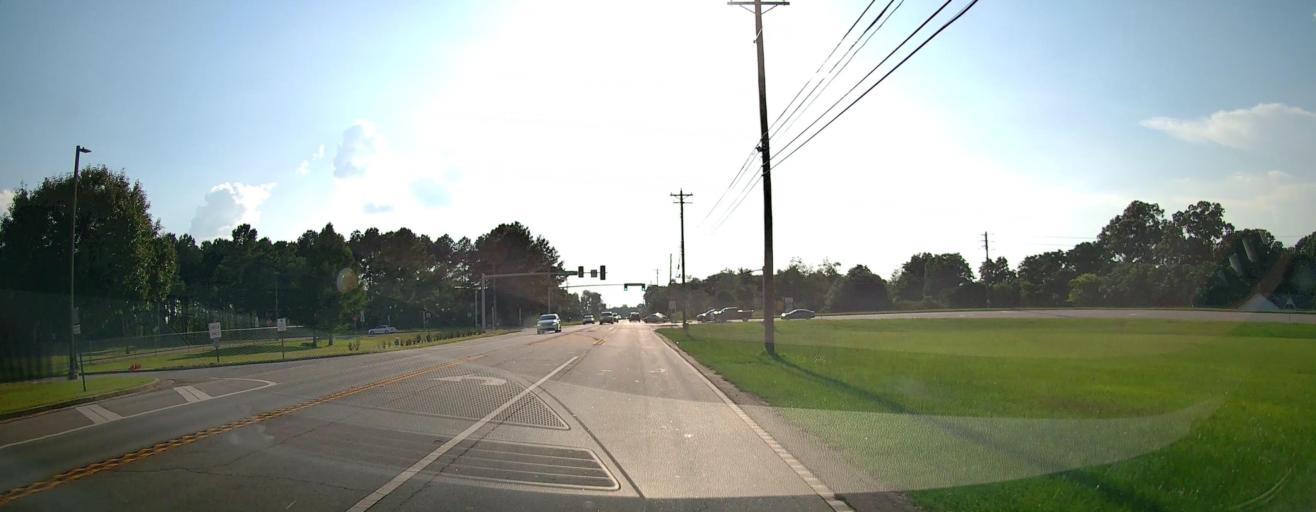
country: US
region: Georgia
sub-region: Houston County
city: Perry
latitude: 32.5062
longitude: -83.6513
